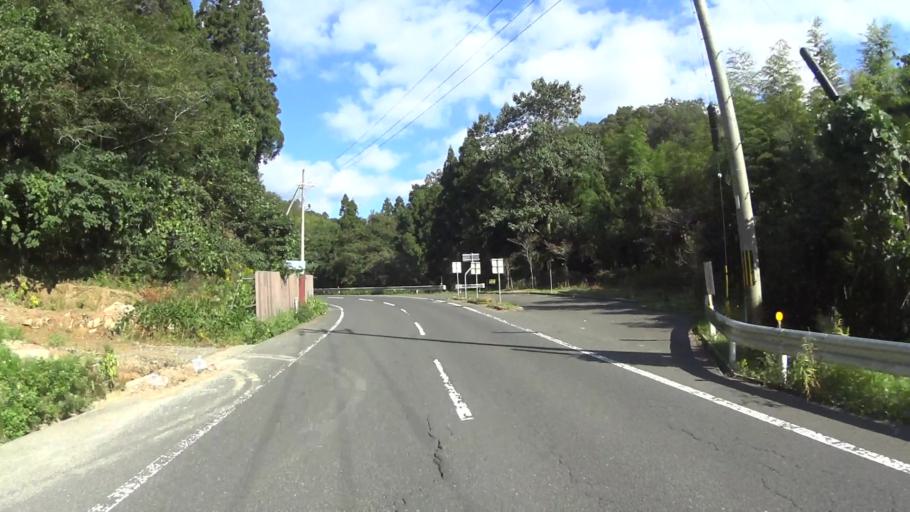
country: JP
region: Kyoto
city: Miyazu
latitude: 35.5904
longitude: 135.1605
